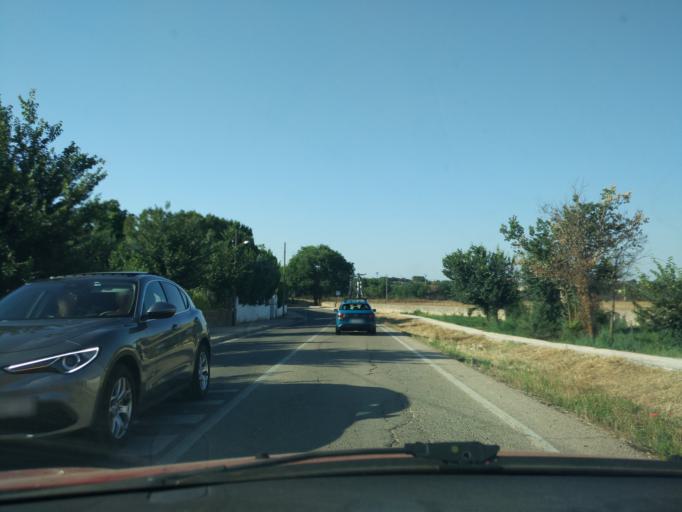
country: ES
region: Madrid
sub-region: Provincia de Madrid
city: Nuevo Baztan
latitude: 40.3689
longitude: -3.2445
